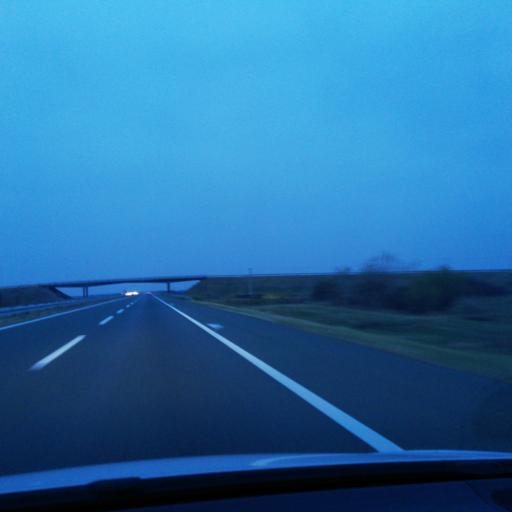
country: RS
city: Sasinci
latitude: 44.9754
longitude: 19.7472
